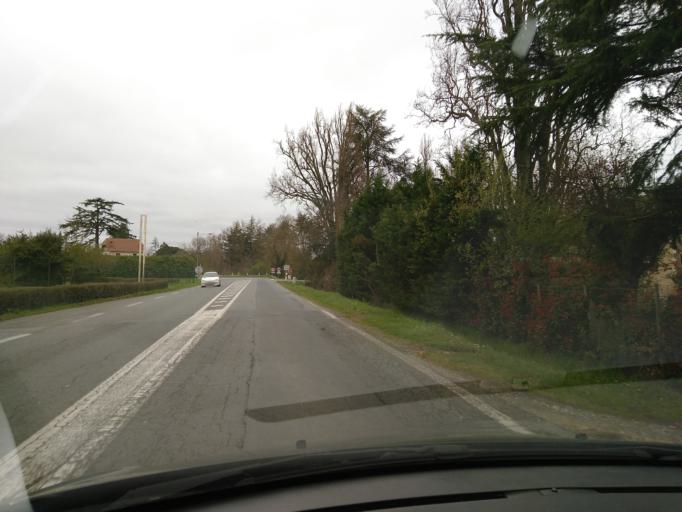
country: FR
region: Aquitaine
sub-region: Departement de la Dordogne
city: Bergerac
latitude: 44.8355
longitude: 0.4941
